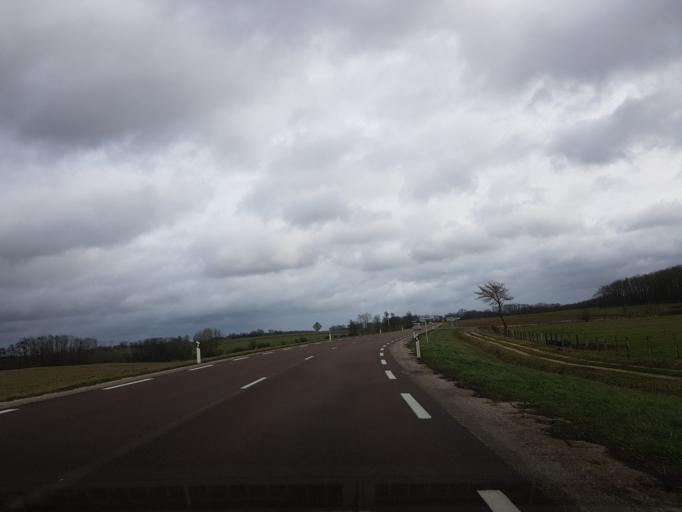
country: FR
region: Champagne-Ardenne
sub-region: Departement de la Haute-Marne
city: Chalindrey
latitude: 47.8458
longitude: 5.4453
